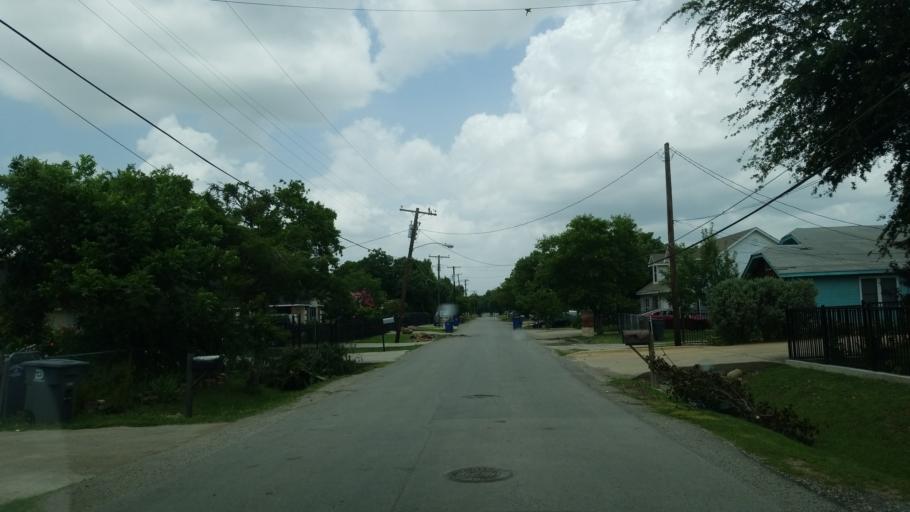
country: US
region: Texas
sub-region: Dallas County
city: Cockrell Hill
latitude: 32.7817
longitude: -96.8953
